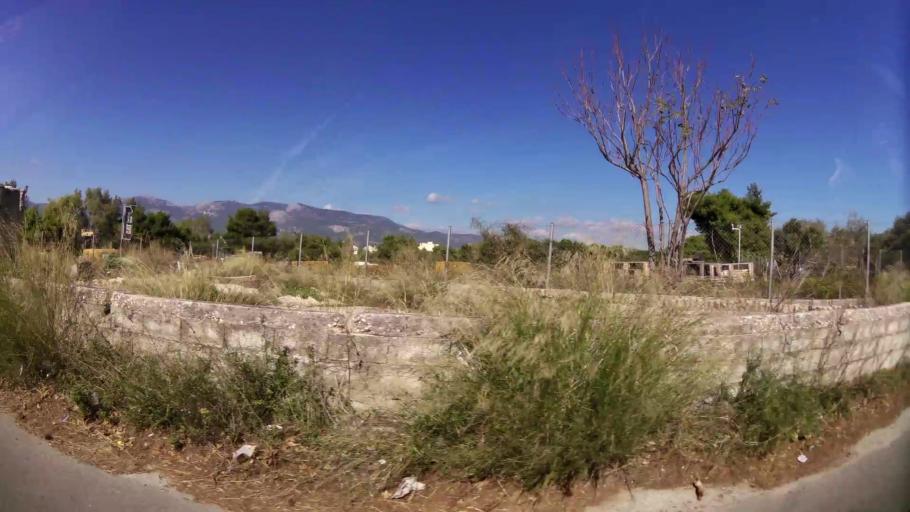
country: GR
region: Attica
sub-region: Nomarchia Athinas
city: Lykovrysi
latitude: 38.0902
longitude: 23.7880
